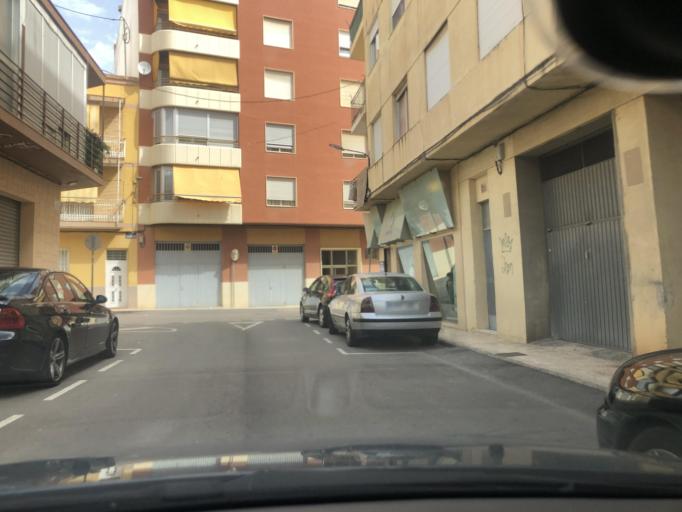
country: ES
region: Valencia
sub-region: Provincia de Alicante
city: Callosa d'En Sarria
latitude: 38.6500
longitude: -0.1200
